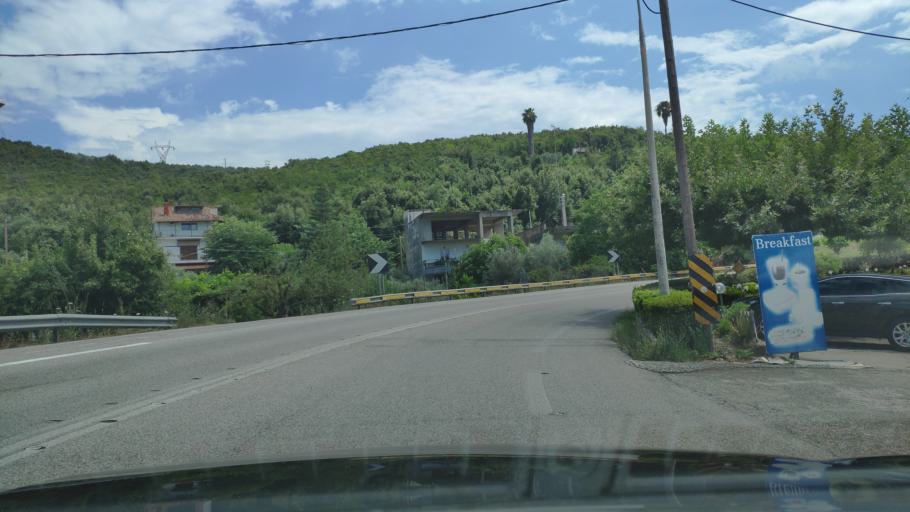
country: GR
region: West Greece
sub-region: Nomos Aitolias kai Akarnanias
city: Menidi
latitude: 39.0405
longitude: 21.1215
